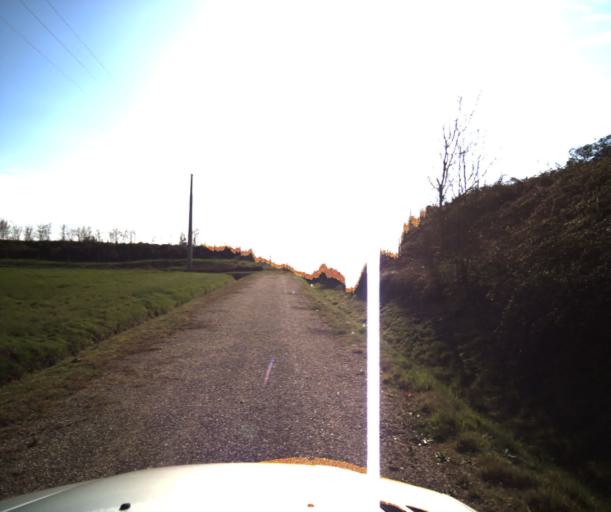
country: FR
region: Midi-Pyrenees
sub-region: Departement du Tarn-et-Garonne
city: Campsas
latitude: 43.9318
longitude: 1.3059
